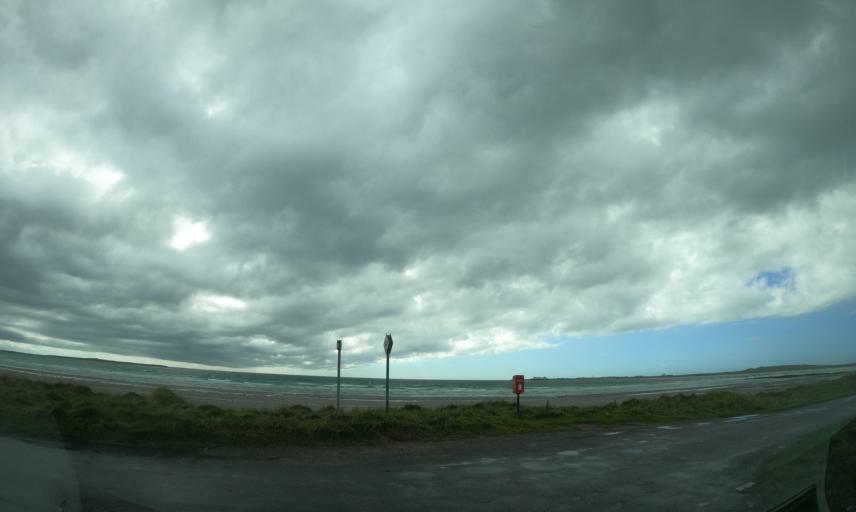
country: GB
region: Scotland
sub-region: Eilean Siar
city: Barra
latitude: 56.5268
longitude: -6.7926
